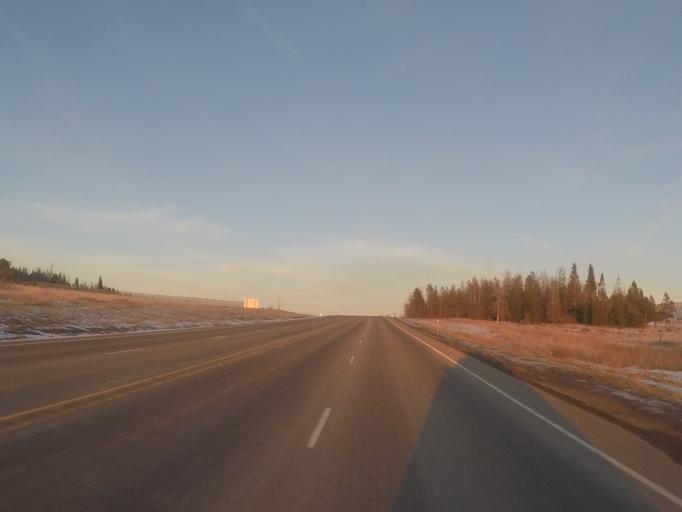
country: US
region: Montana
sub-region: Lewis and Clark County
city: Helena West Side
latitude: 46.5594
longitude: -112.3151
